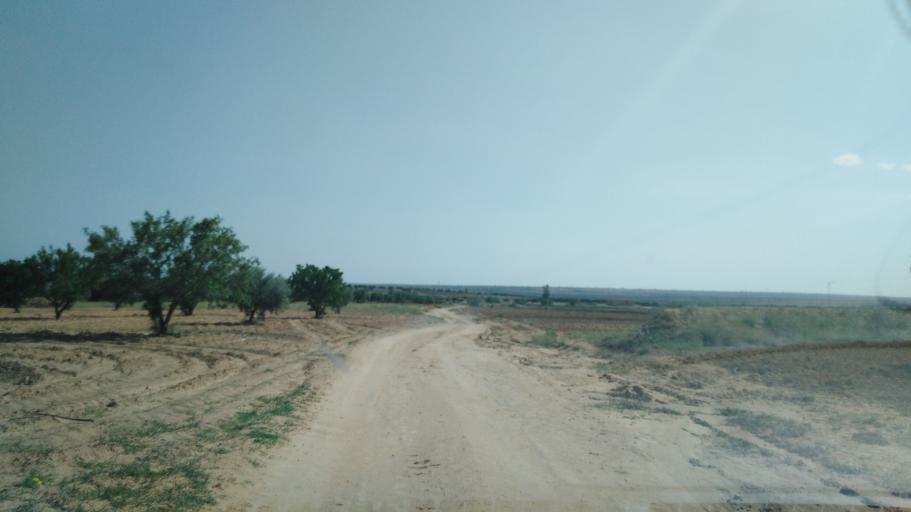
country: TN
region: Safaqis
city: Bi'r `Ali Bin Khalifah
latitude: 34.7933
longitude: 10.3721
